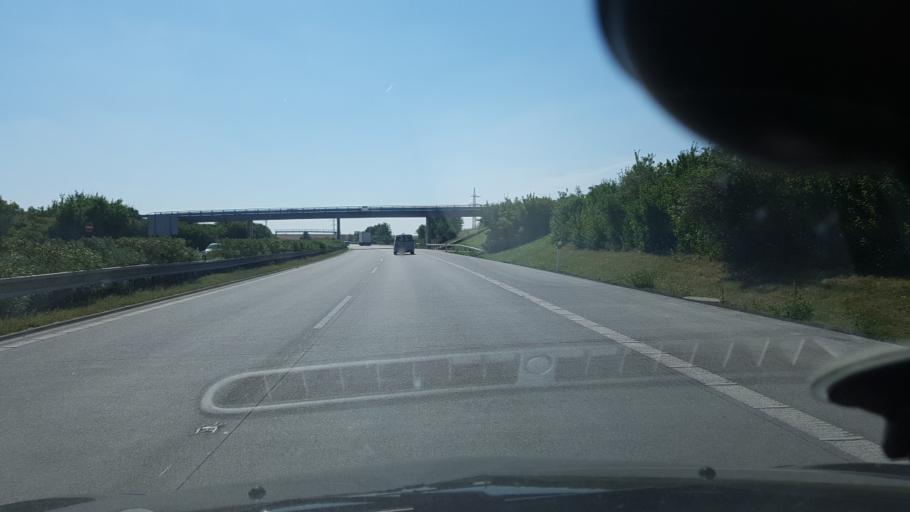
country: CZ
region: Olomoucky
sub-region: Okres Olomouc
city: Olomouc
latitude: 49.5529
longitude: 17.2284
